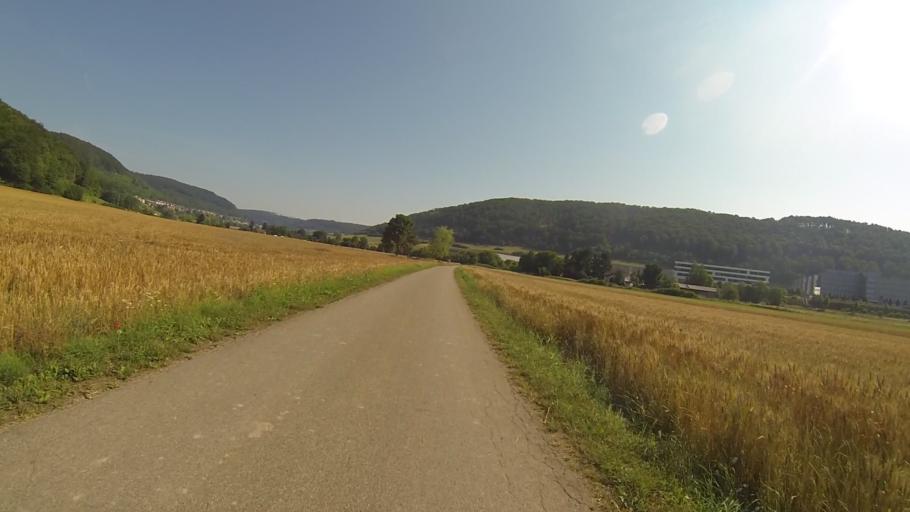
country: DE
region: Baden-Wuerttemberg
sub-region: Regierungsbezirk Stuttgart
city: Oberkochen
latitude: 48.7652
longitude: 10.0981
